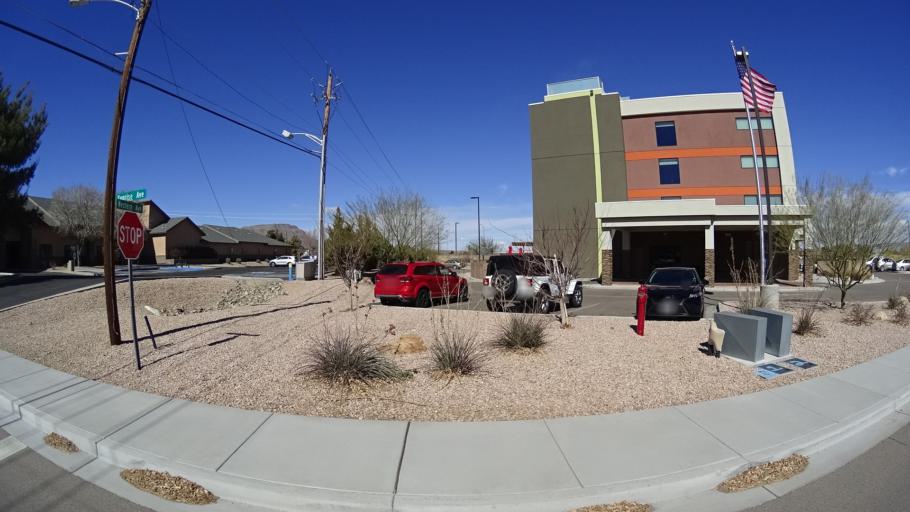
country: US
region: Arizona
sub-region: Mohave County
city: Kingman
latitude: 35.2149
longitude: -114.0400
